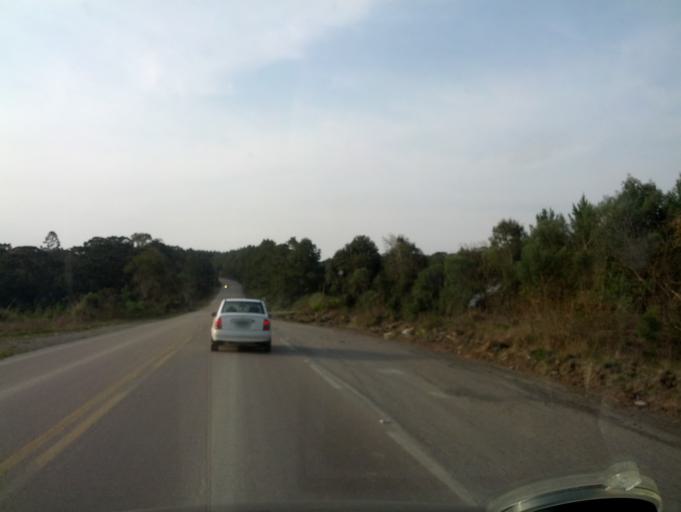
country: BR
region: Santa Catarina
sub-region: Otacilio Costa
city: Otacilio Costa
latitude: -27.4587
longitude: -50.1229
